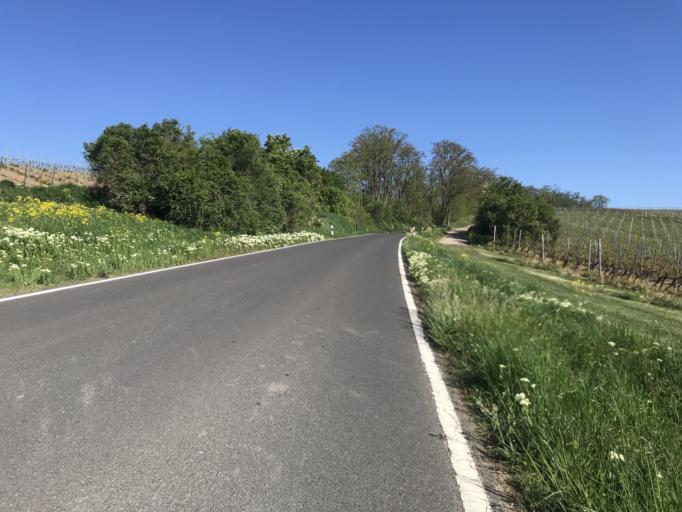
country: DE
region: Rheinland-Pfalz
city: Zornheim
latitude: 49.8754
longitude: 8.2164
